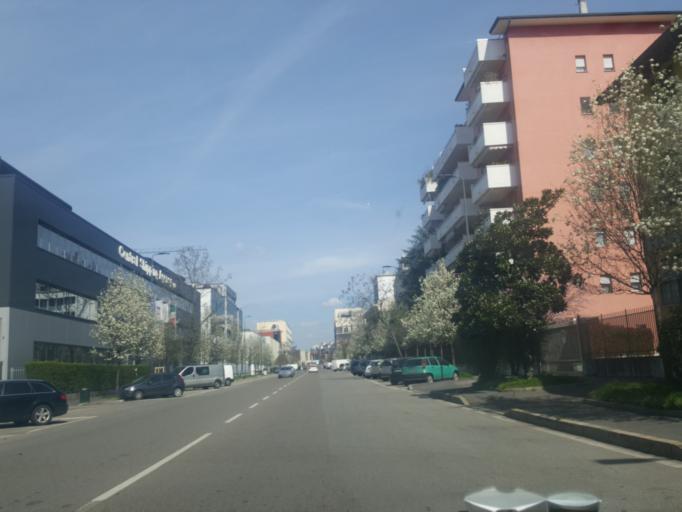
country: IT
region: Lombardy
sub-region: Citta metropolitana di Milano
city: Novate Milanese
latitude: 45.4972
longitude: 9.1392
